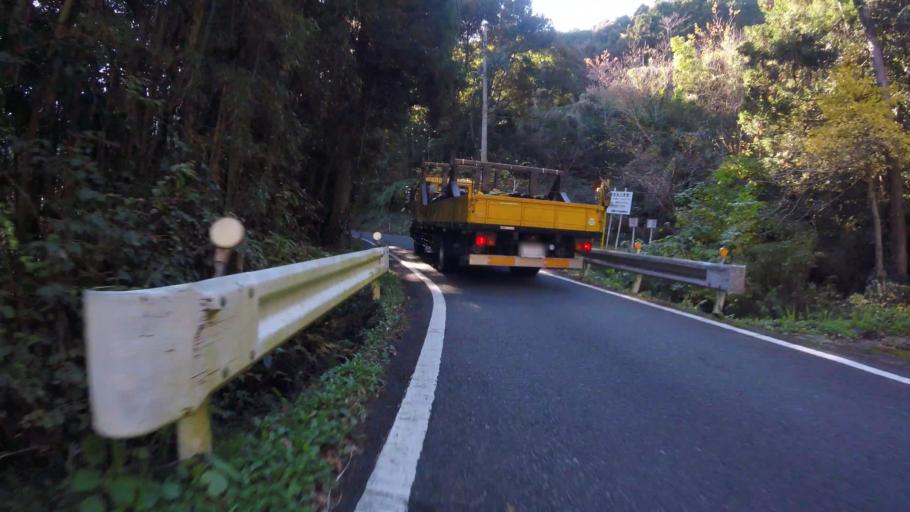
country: JP
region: Shizuoka
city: Shimoda
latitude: 34.7696
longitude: 138.9594
